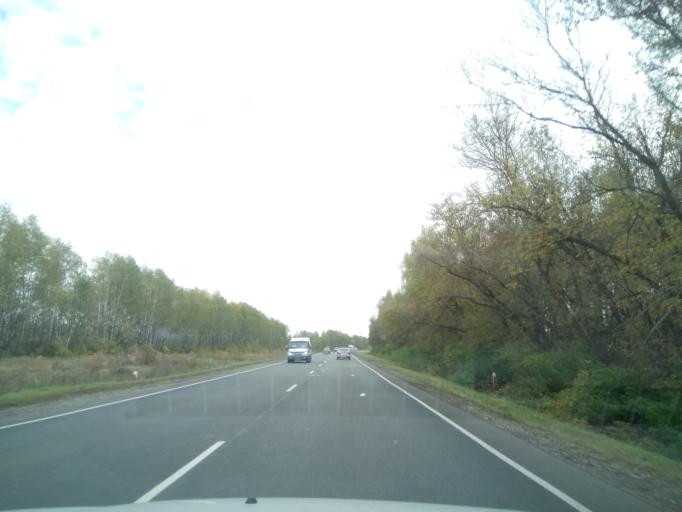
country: RU
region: Nizjnij Novgorod
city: Lukoyanov
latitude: 55.0630
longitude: 44.3555
